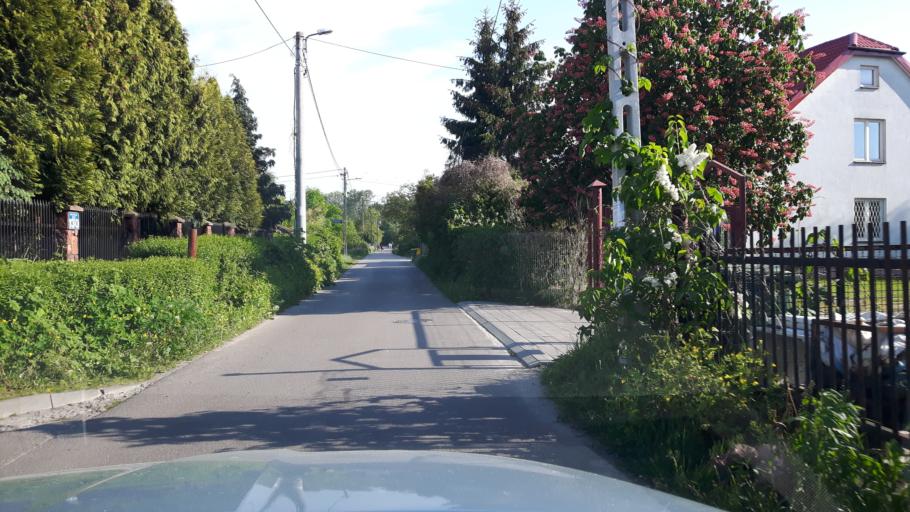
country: PL
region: Masovian Voivodeship
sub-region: Warszawa
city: Praga Poludnie
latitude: 52.2553
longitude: 21.1209
